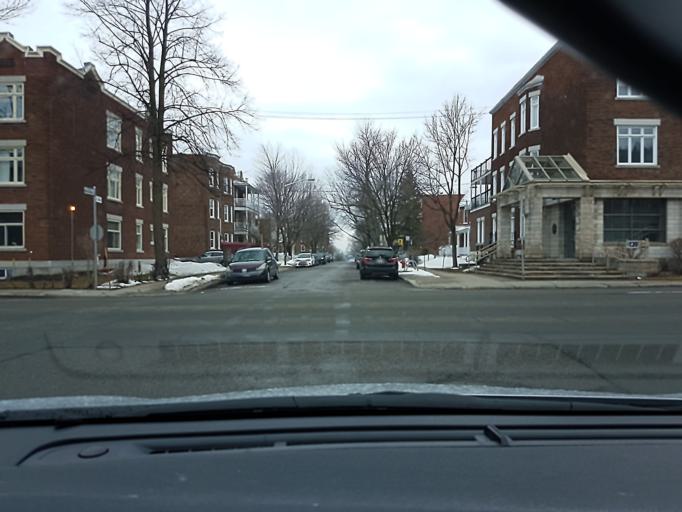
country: CA
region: Quebec
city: Quebec
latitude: 46.7988
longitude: -71.2359
